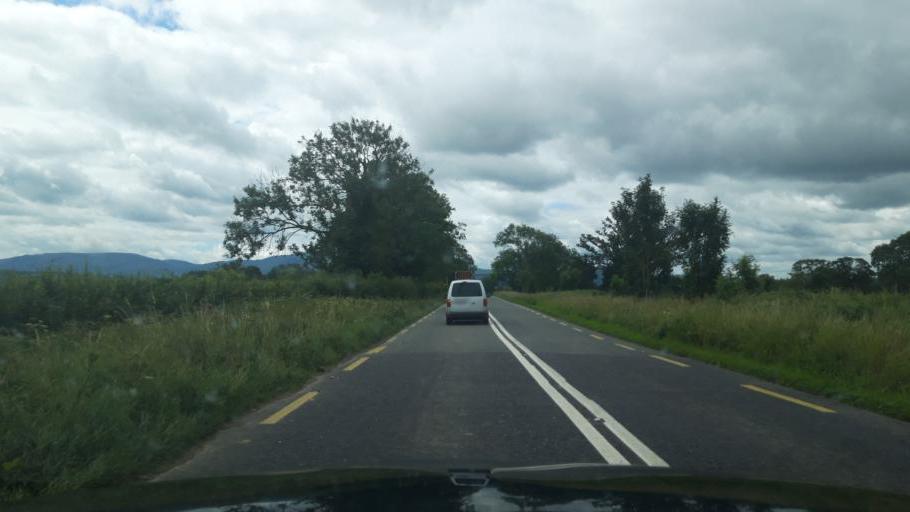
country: IE
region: Munster
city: Carrick-on-Suir
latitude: 52.3976
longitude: -7.4963
